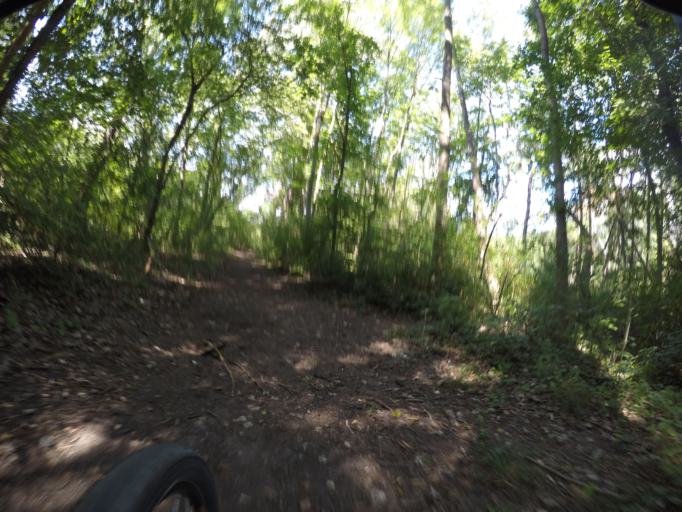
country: AT
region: Lower Austria
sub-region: Politischer Bezirk Wien-Umgebung
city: Schwechat
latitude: 48.1849
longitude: 16.4889
